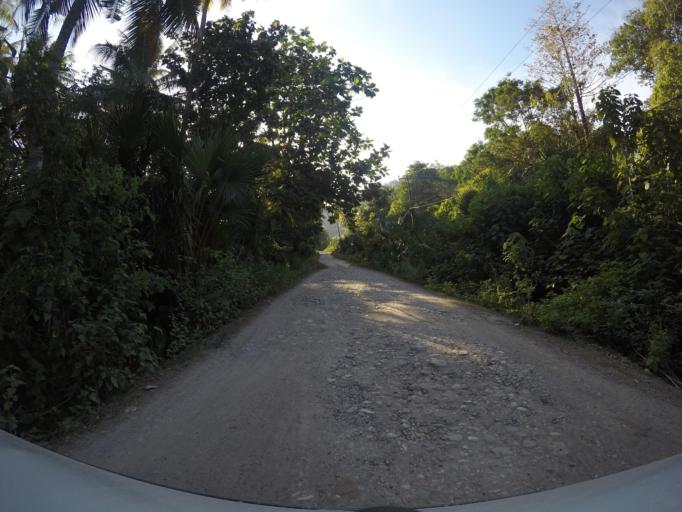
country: TL
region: Viqueque
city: Viqueque
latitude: -8.8039
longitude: 126.5702
